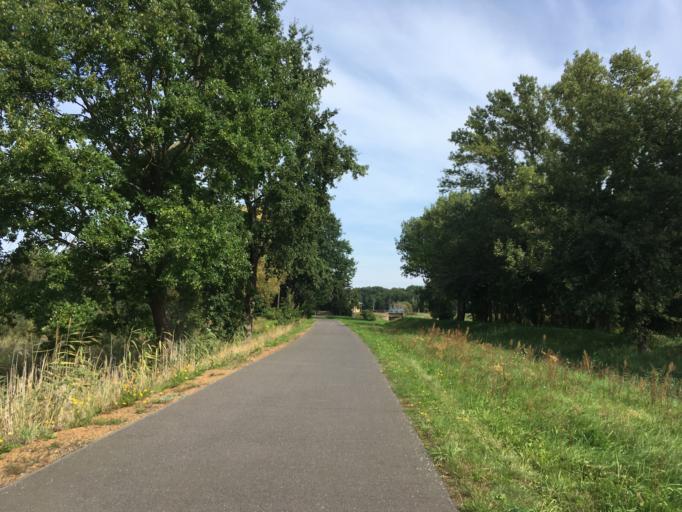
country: DE
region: Brandenburg
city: Forst
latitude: 51.8030
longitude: 14.6027
